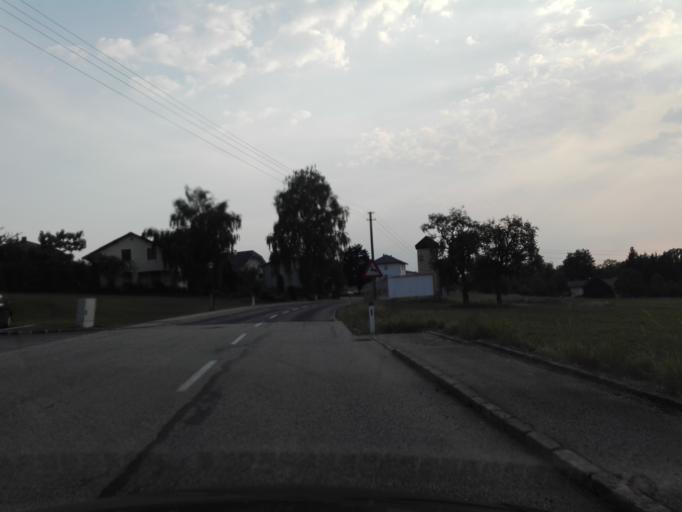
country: AT
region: Upper Austria
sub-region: Politischer Bezirk Grieskirchen
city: Grieskirchen
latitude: 48.2859
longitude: 13.8292
